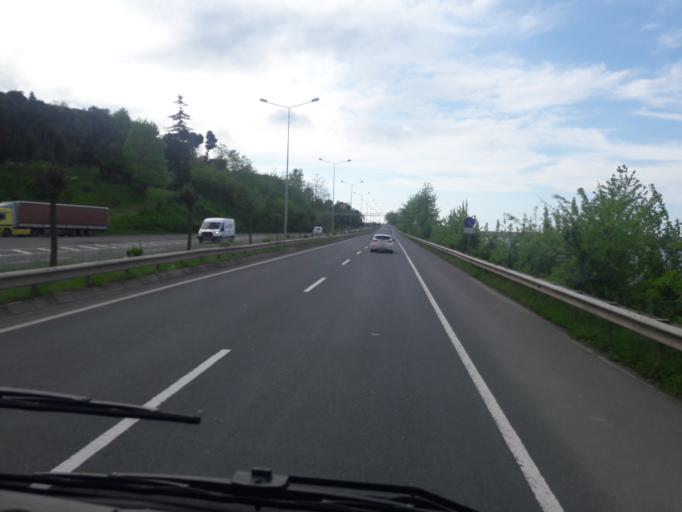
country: TR
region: Giresun
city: Piraziz
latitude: 40.9589
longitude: 38.1089
